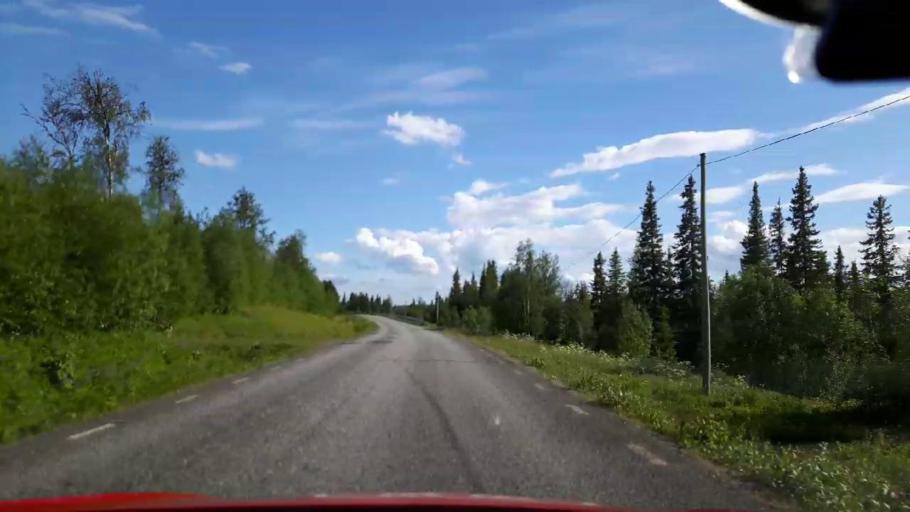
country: SE
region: Jaemtland
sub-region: Krokoms Kommun
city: Valla
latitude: 63.7085
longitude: 14.1419
